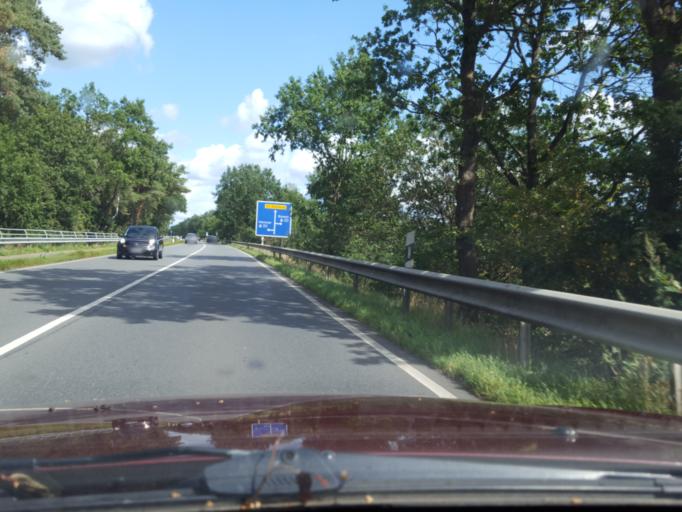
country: DE
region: Lower Saxony
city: Verden
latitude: 52.9559
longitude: 9.2414
